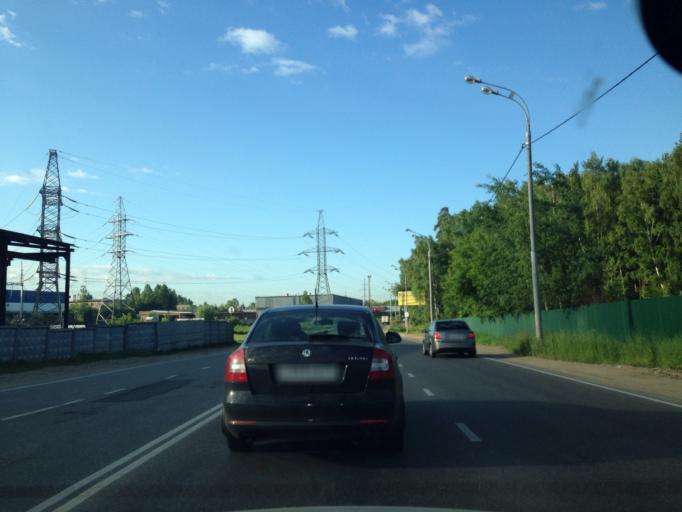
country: RU
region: Moscow
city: Vostochnyy
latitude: 55.7995
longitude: 37.8964
